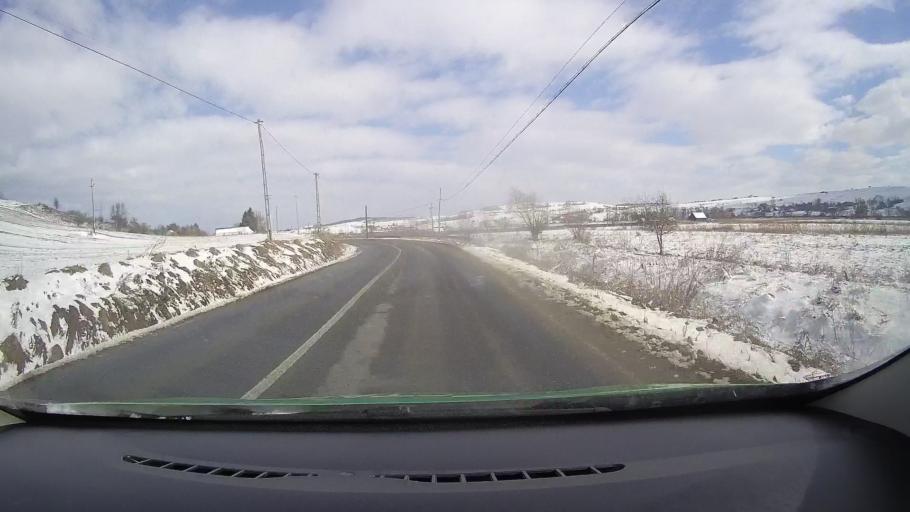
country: RO
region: Sibiu
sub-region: Oras Agnita
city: Agnita
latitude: 45.9648
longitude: 24.5961
